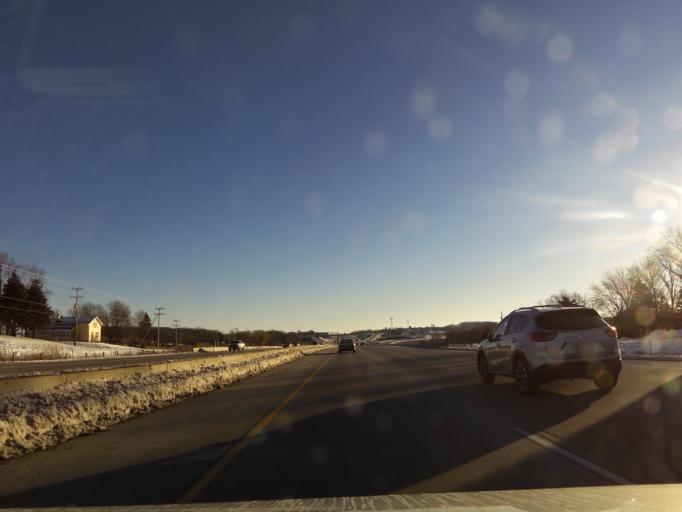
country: US
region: Wisconsin
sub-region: Racine County
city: Caledonia
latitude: 42.8181
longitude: -87.9529
